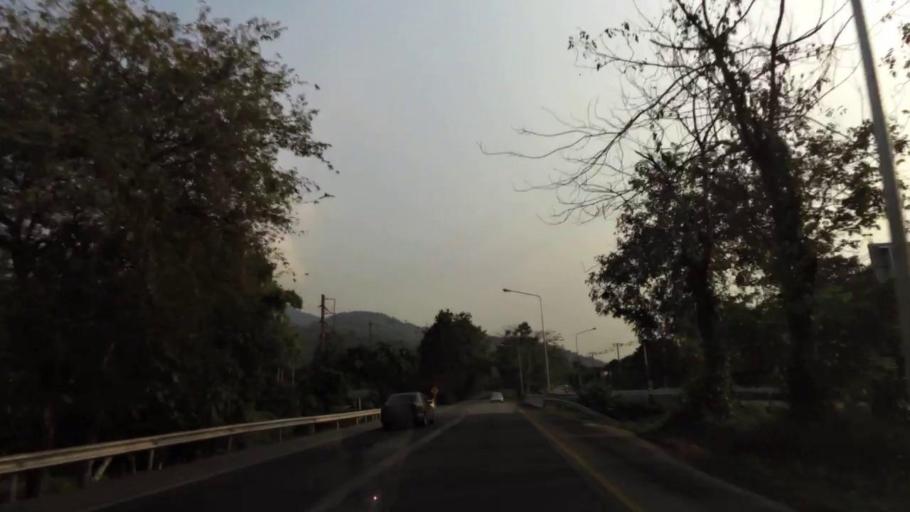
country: TH
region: Chanthaburi
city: Chanthaburi
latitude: 12.5730
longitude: 102.1622
